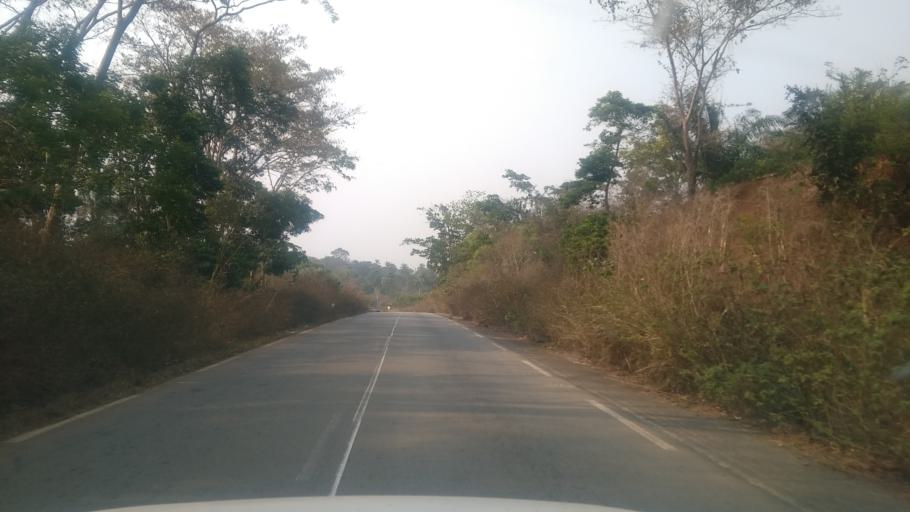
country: CM
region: West
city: Tonga
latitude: 4.9668
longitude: 10.7111
